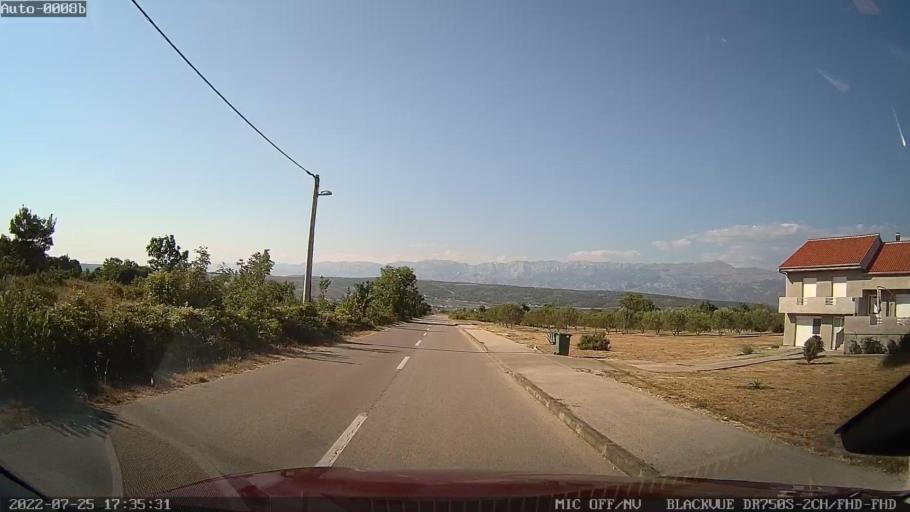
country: HR
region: Zadarska
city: Posedarje
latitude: 44.1915
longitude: 15.4726
